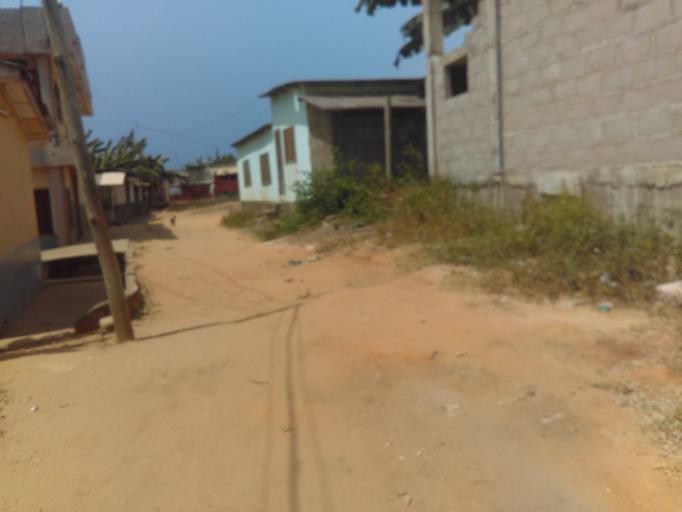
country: GH
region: Central
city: Cape Coast
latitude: 5.1052
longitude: -1.2892
